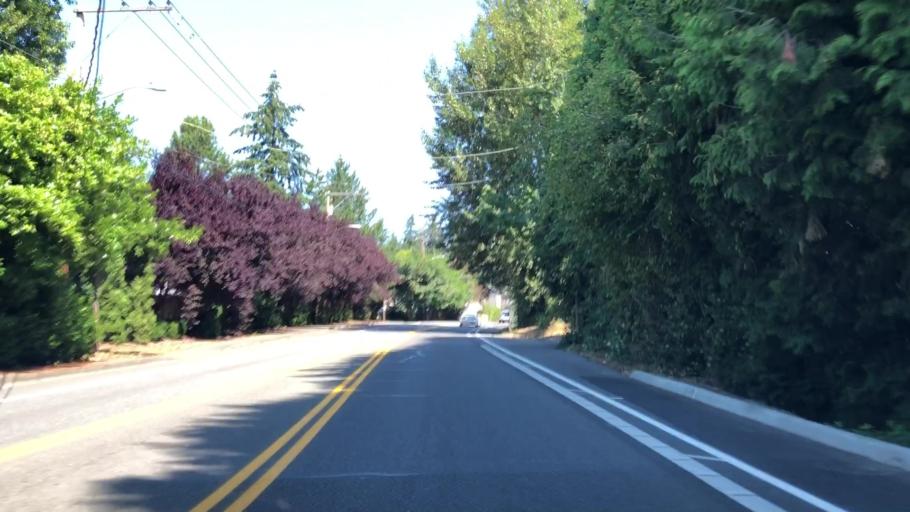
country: US
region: Washington
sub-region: King County
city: Inglewood-Finn Hill
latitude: 47.7107
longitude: -122.2381
